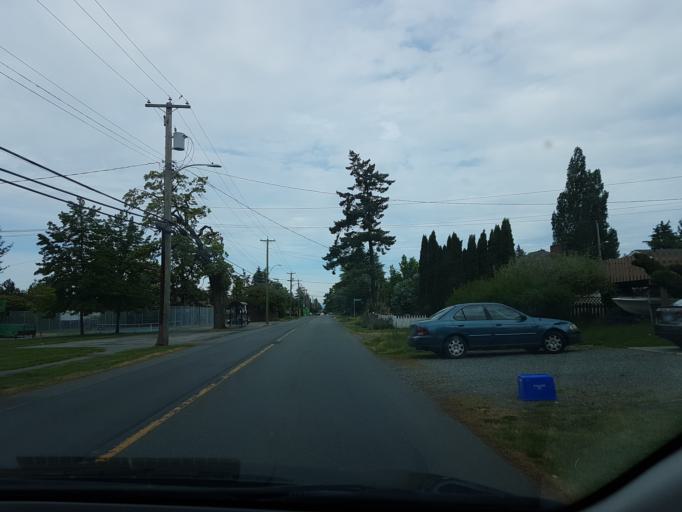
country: CA
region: British Columbia
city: Oak Bay
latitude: 48.4864
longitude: -123.3321
